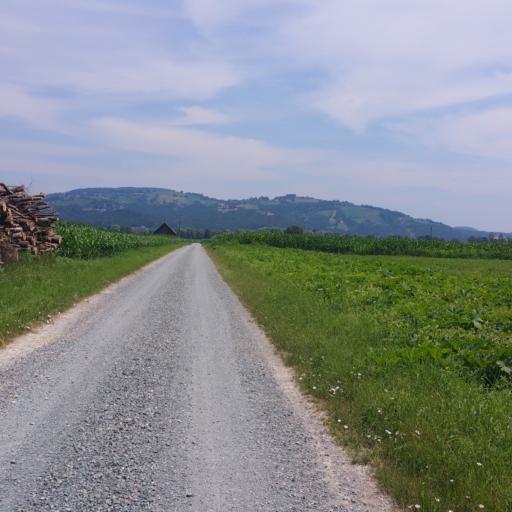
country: AT
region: Styria
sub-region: Politischer Bezirk Leibnitz
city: Gleinstatten
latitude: 46.7496
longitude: 15.3736
